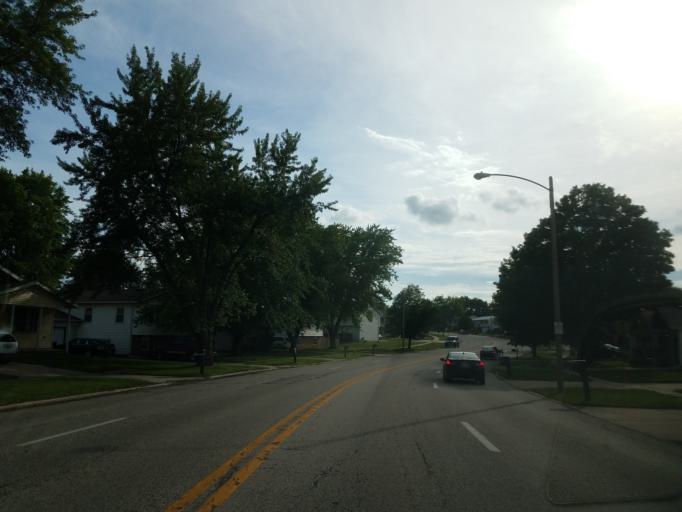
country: US
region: Illinois
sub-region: McLean County
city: Normal
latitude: 40.4980
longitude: -88.9399
